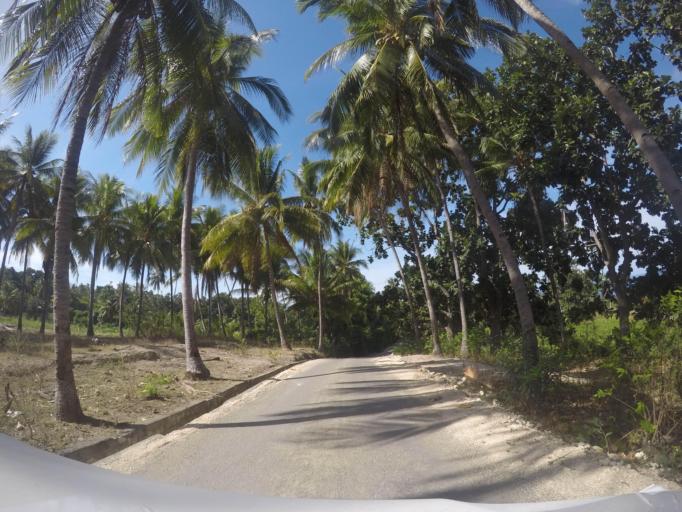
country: TL
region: Baucau
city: Baucau
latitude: -8.4541
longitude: 126.4580
